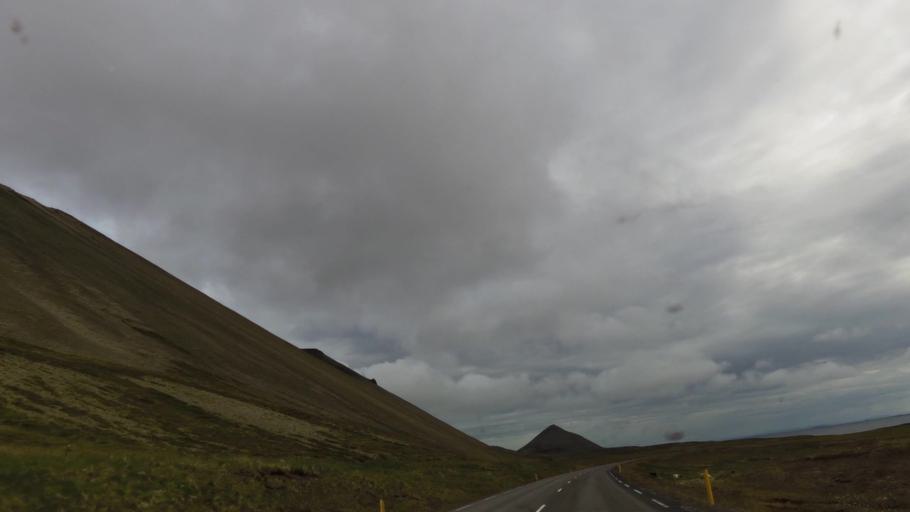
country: IS
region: West
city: Stykkisholmur
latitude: 64.9574
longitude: -23.1531
